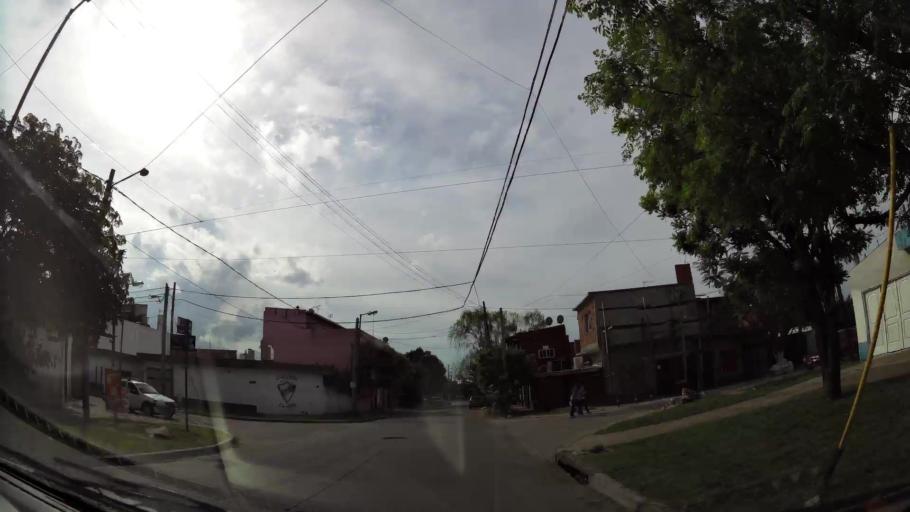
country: AR
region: Buenos Aires
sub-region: Partido de Quilmes
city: Quilmes
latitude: -34.7499
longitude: -58.2804
